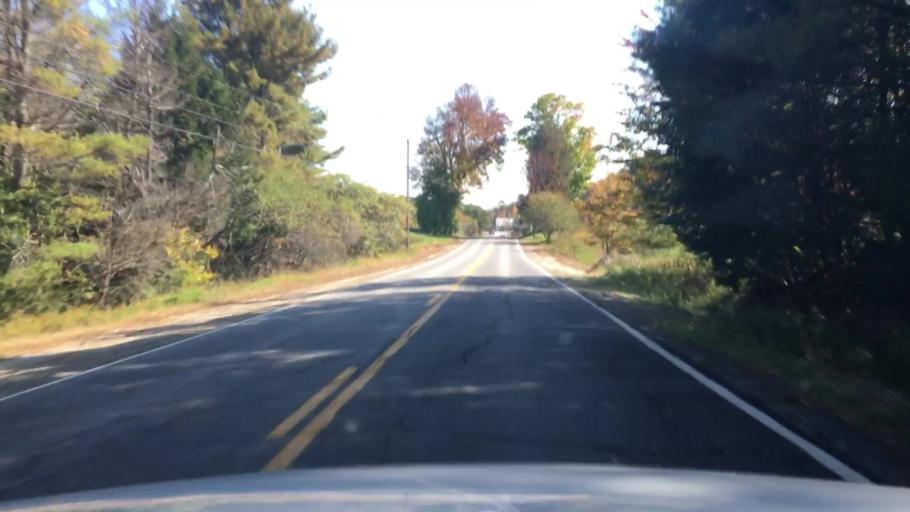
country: US
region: Maine
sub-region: Androscoggin County
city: Lisbon Falls
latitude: 44.0369
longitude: -69.9786
